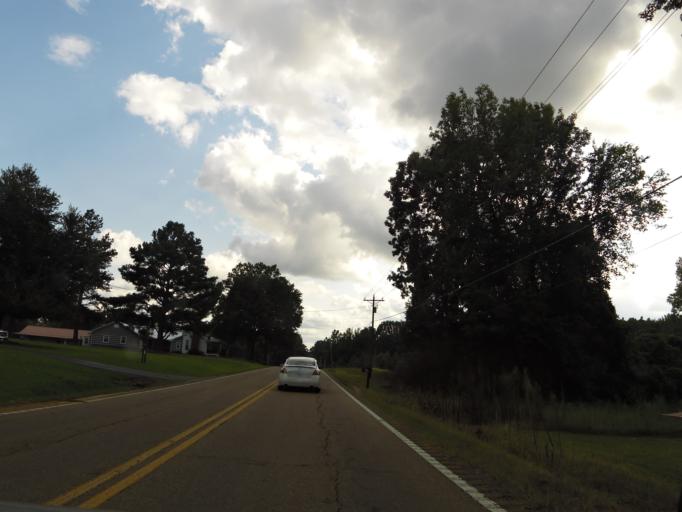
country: US
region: Mississippi
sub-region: Alcorn County
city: Farmington
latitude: 35.0177
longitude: -88.4563
